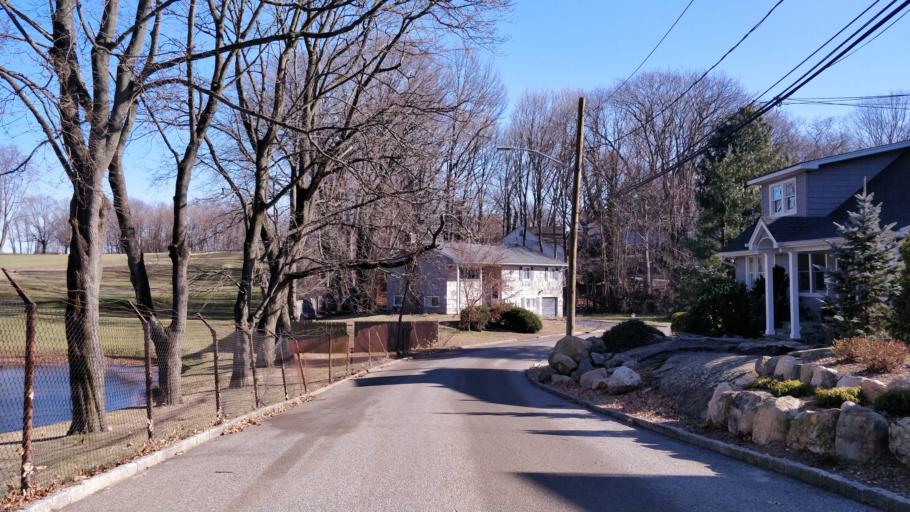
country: US
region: New York
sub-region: Nassau County
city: Glen Head
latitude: 40.8412
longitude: -73.6213
